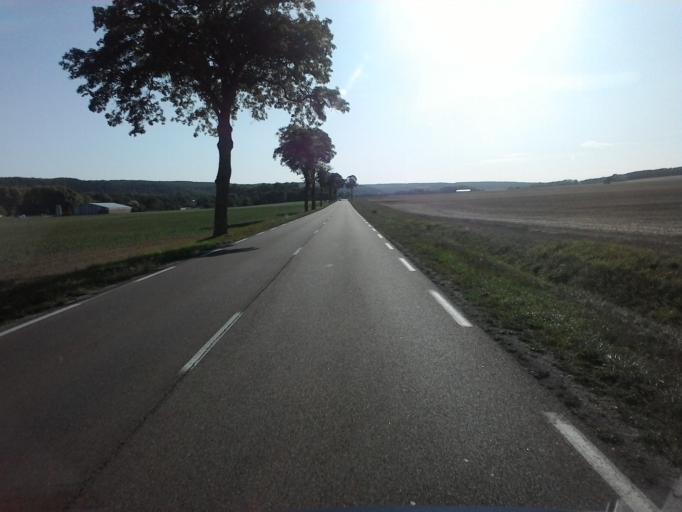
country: FR
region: Champagne-Ardenne
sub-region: Departement de l'Aube
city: Bar-sur-Seine
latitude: 48.1279
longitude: 4.3488
